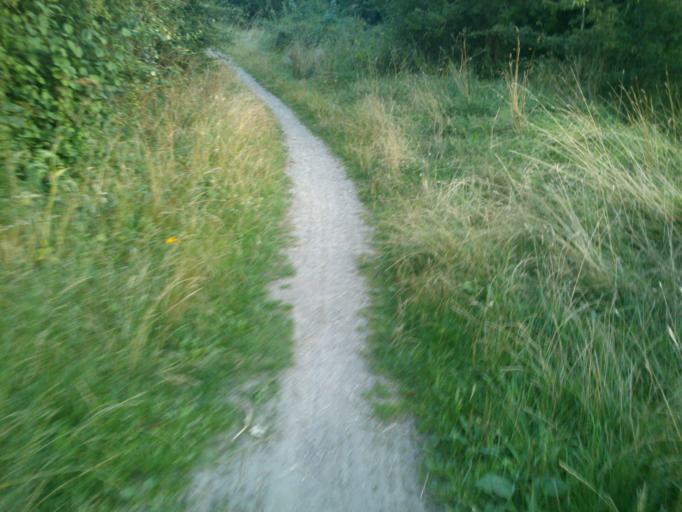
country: DK
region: South Denmark
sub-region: Fredericia Kommune
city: Fredericia
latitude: 55.5742
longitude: 9.7167
